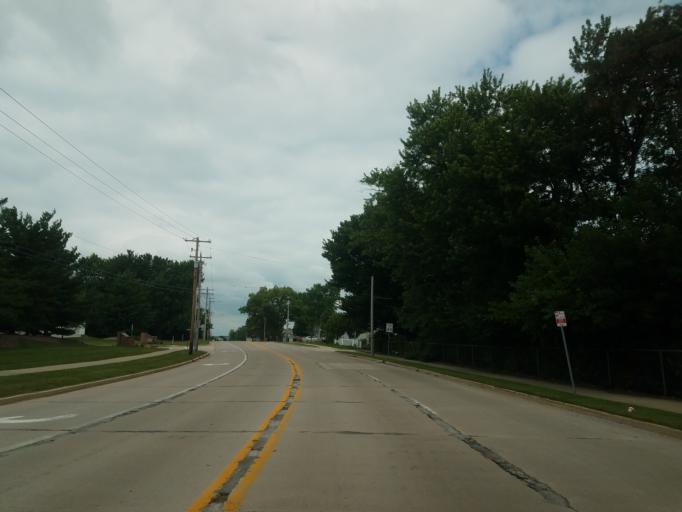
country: US
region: Illinois
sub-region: McLean County
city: Bloomington
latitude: 40.4513
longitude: -89.0298
